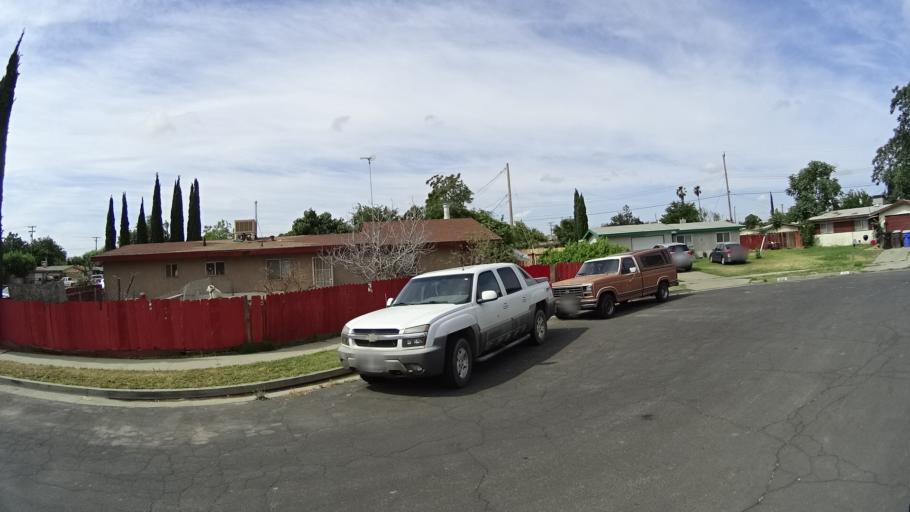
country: US
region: California
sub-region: Kings County
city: Hanford
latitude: 36.3154
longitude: -119.6661
